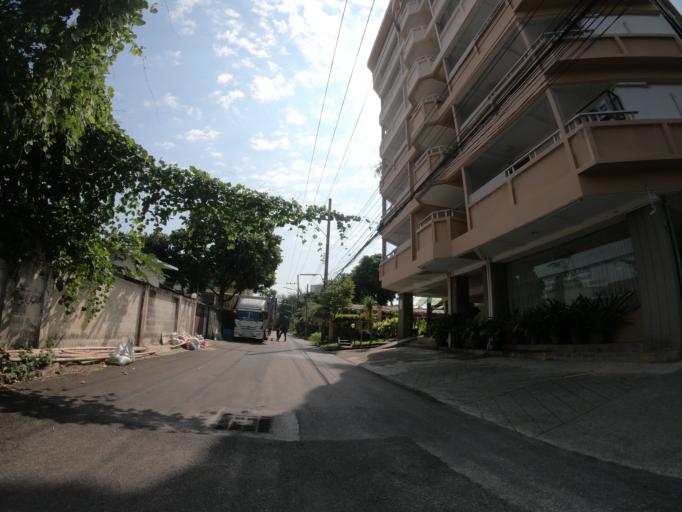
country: TH
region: Chiang Mai
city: Chiang Mai
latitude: 18.8058
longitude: 99.0146
